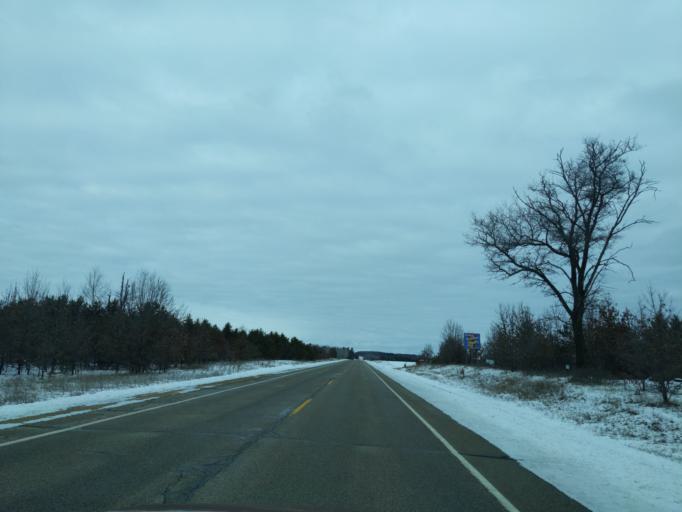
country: US
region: Wisconsin
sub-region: Waushara County
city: Wautoma
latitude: 43.9857
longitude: -89.3276
